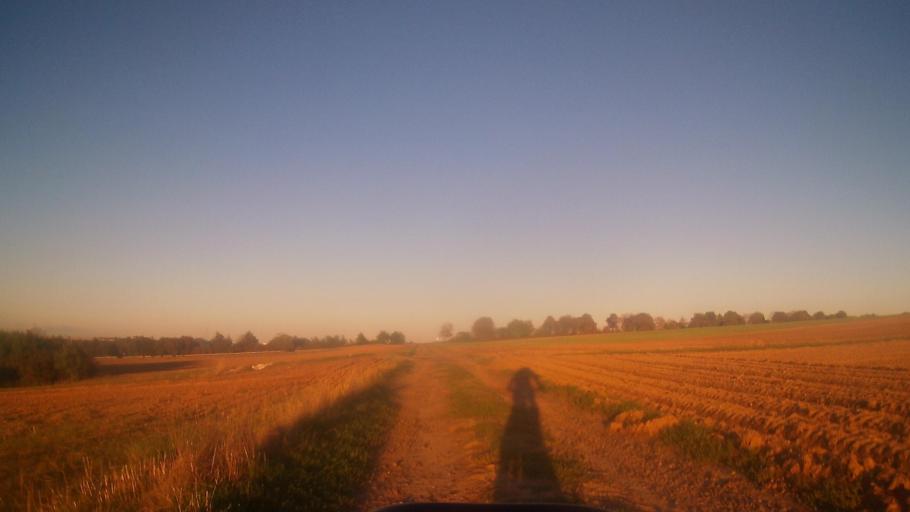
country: DE
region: Rheinland-Pfalz
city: Morstadt
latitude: 49.6271
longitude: 8.2767
